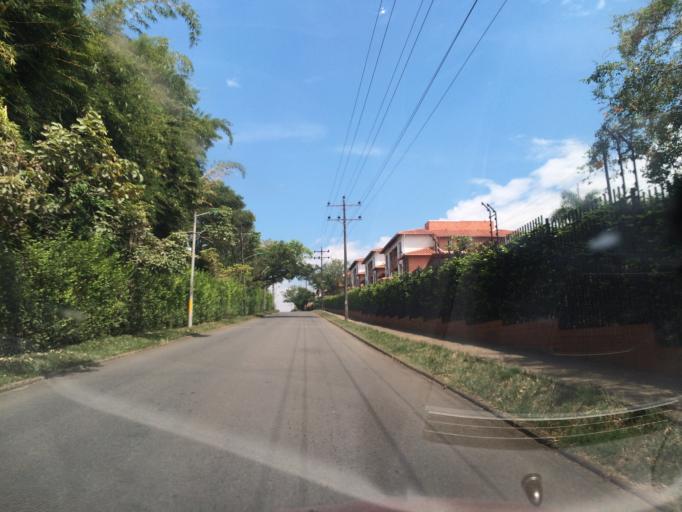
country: CO
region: Valle del Cauca
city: Jamundi
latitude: 3.3481
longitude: -76.5472
